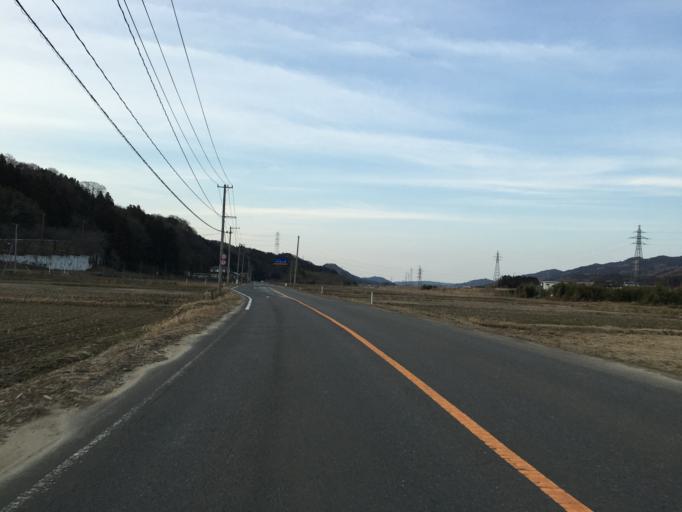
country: JP
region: Ibaraki
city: Daigo
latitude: 36.8790
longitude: 140.4150
